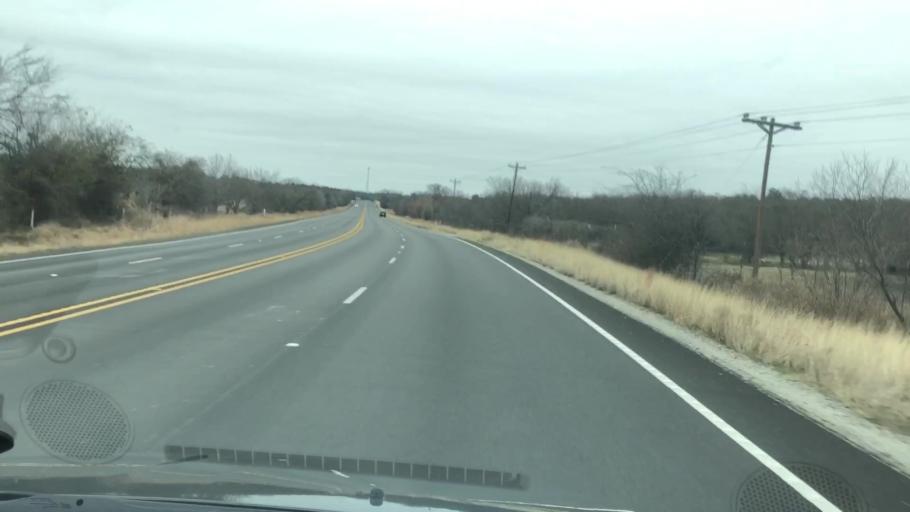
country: US
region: Texas
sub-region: Erath County
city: Stephenville
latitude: 32.4331
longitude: -98.1402
